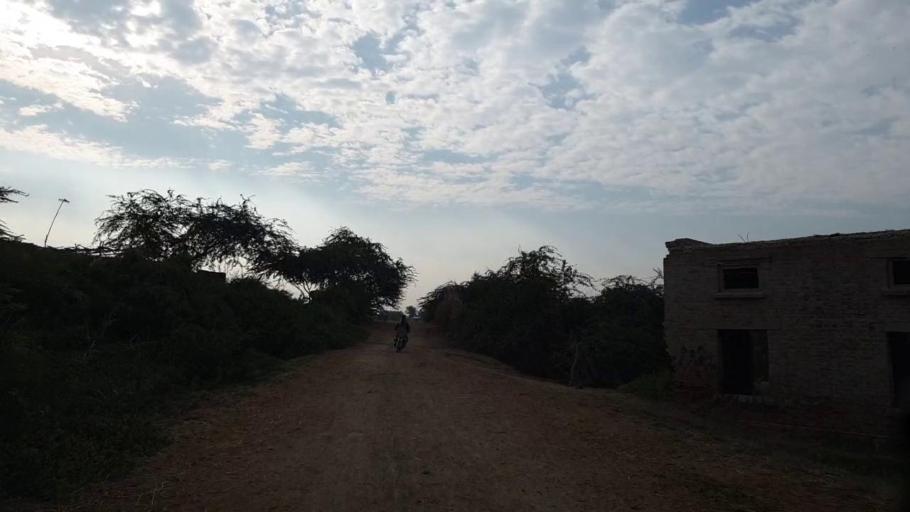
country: PK
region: Sindh
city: Tando Muhammad Khan
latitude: 25.0961
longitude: 68.4148
